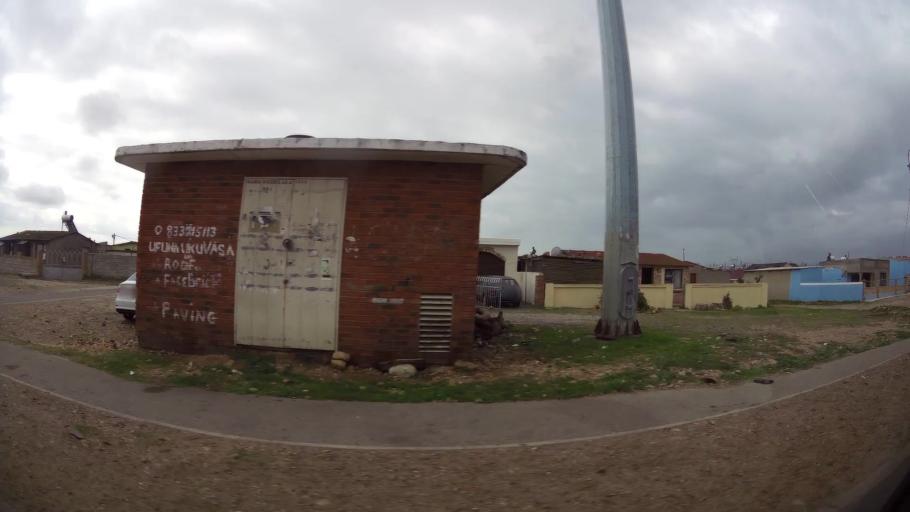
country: ZA
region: Eastern Cape
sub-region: Nelson Mandela Bay Metropolitan Municipality
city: Port Elizabeth
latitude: -33.8840
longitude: 25.6038
